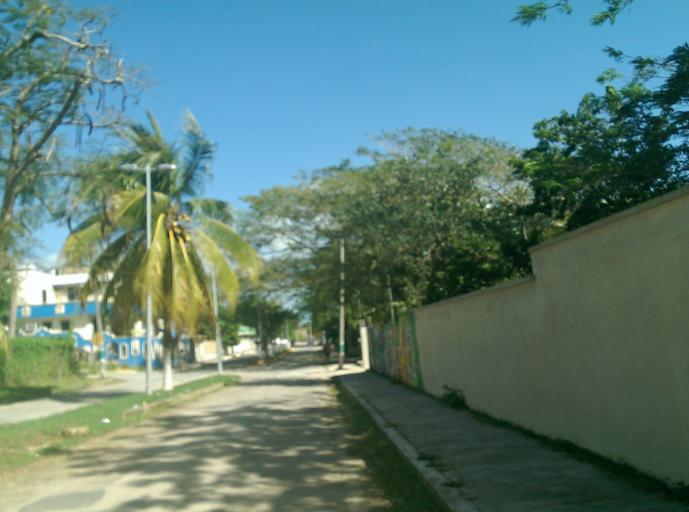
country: MX
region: Quintana Roo
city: Bacalar
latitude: 18.6747
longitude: -88.3894
